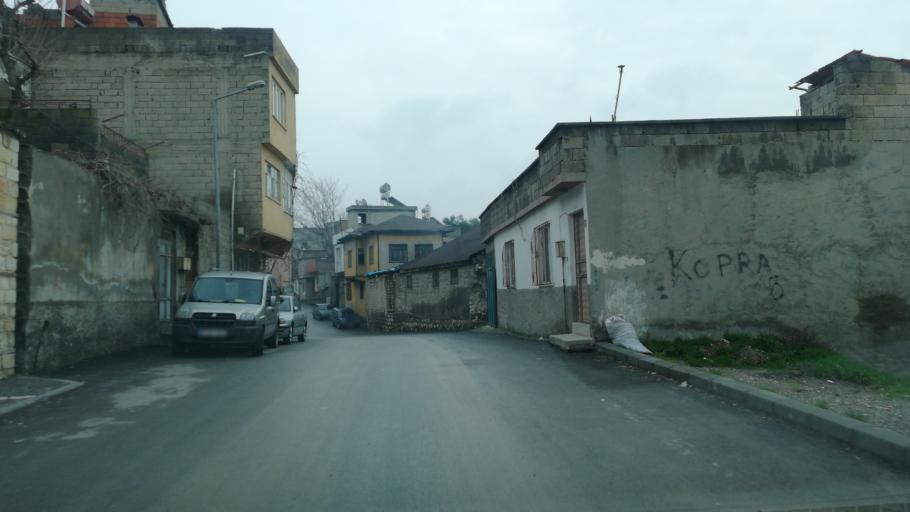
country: TR
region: Kahramanmaras
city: Kahramanmaras
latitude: 37.5816
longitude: 36.9341
